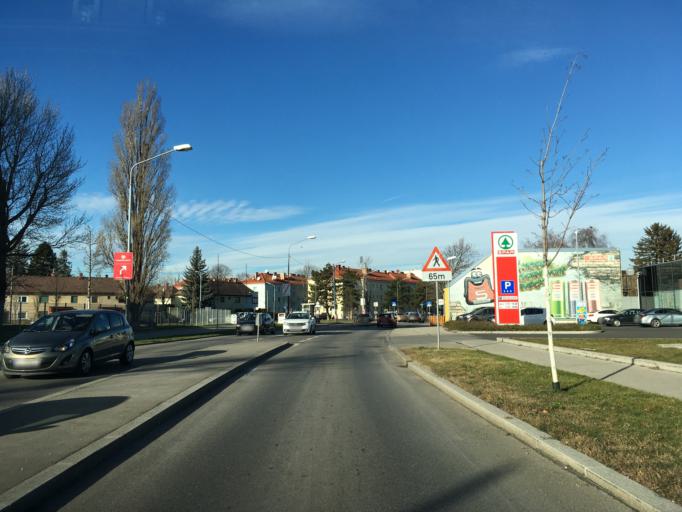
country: AT
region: Lower Austria
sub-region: Politischer Bezirk Wien-Umgebung
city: Gerasdorf bei Wien
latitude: 48.2462
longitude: 16.4524
